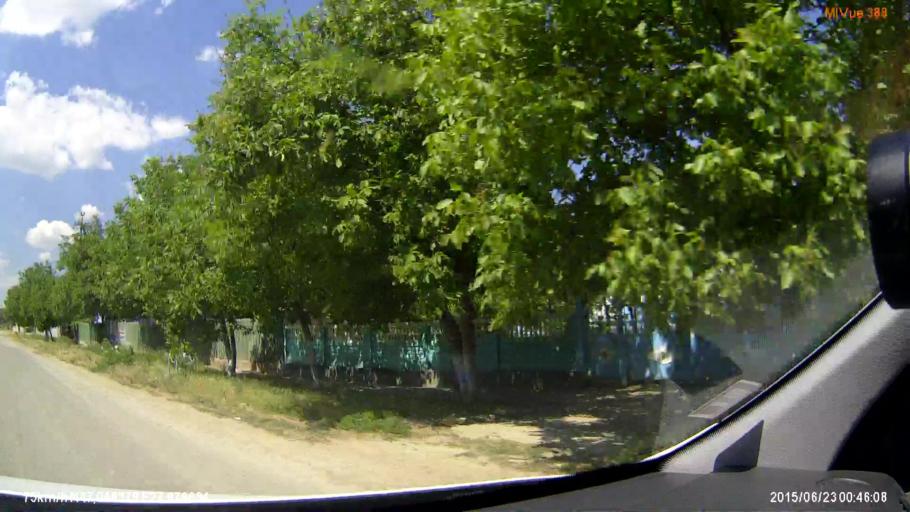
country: RO
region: Iasi
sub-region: Comuna Grozesti
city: Grozesti
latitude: 47.0463
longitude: 27.9768
